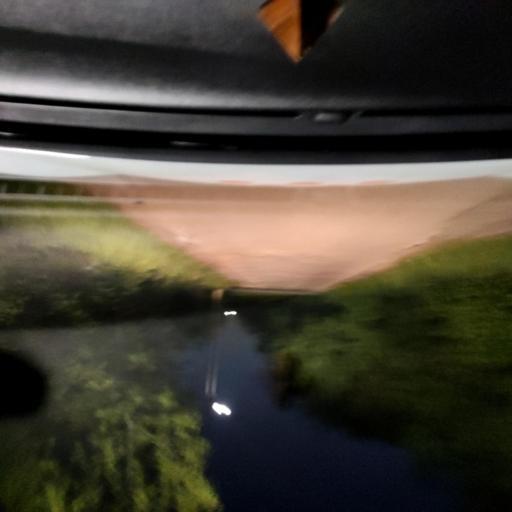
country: RU
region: Tatarstan
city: Staroye Arakchino
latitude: 55.8089
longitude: 48.9204
